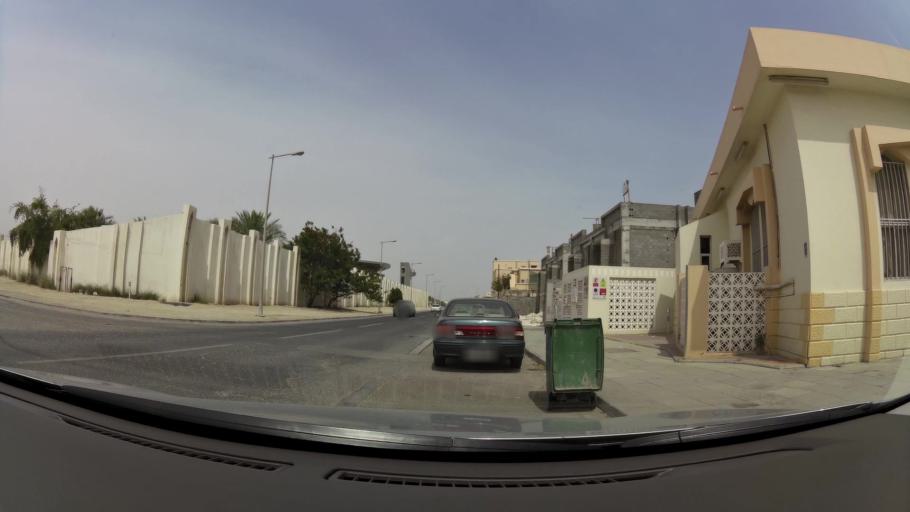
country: QA
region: Baladiyat ad Dawhah
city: Doha
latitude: 25.2684
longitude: 51.4925
